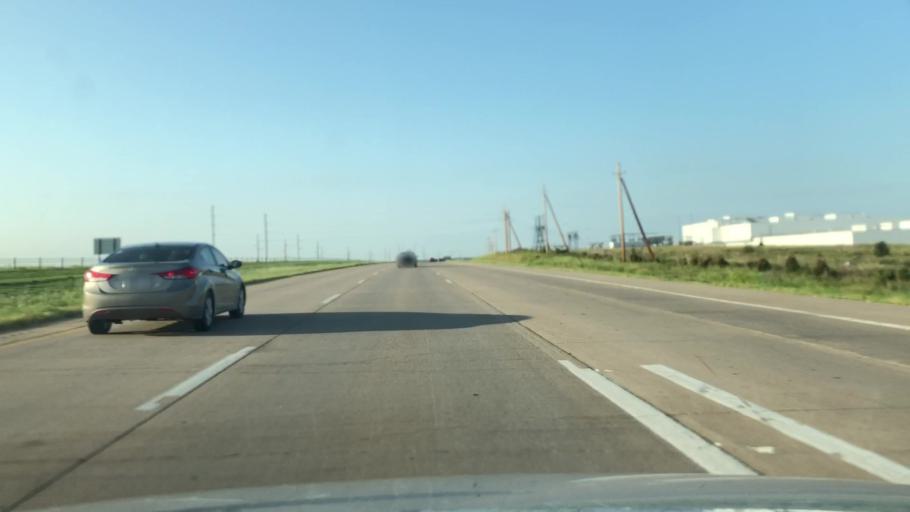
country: US
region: Oklahoma
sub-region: Washington County
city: Bartlesville
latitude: 36.5796
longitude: -95.9302
